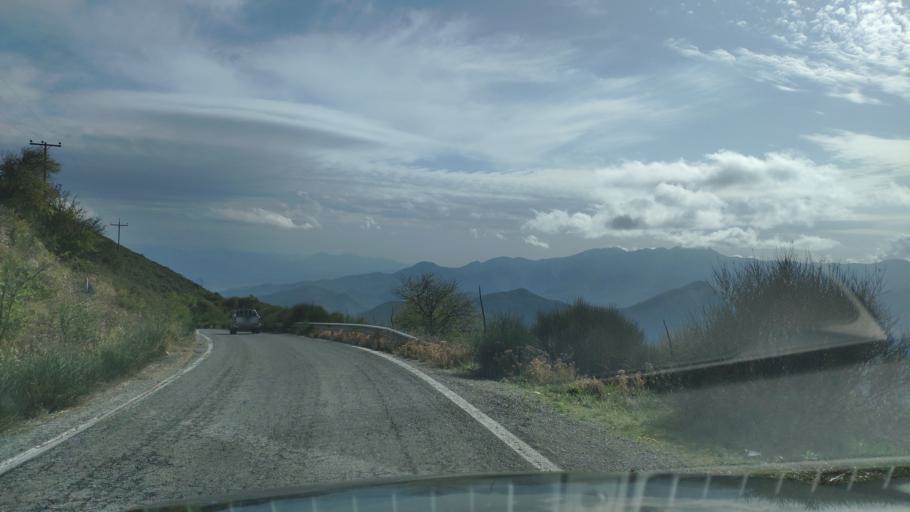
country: GR
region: Peloponnese
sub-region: Nomos Arkadias
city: Dimitsana
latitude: 37.5754
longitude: 22.0184
